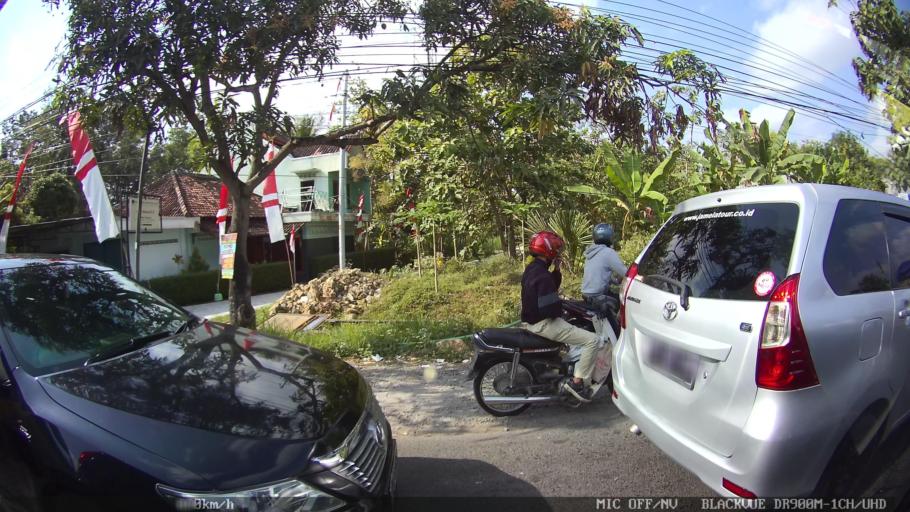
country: ID
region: Daerah Istimewa Yogyakarta
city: Godean
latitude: -7.8273
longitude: 110.2234
